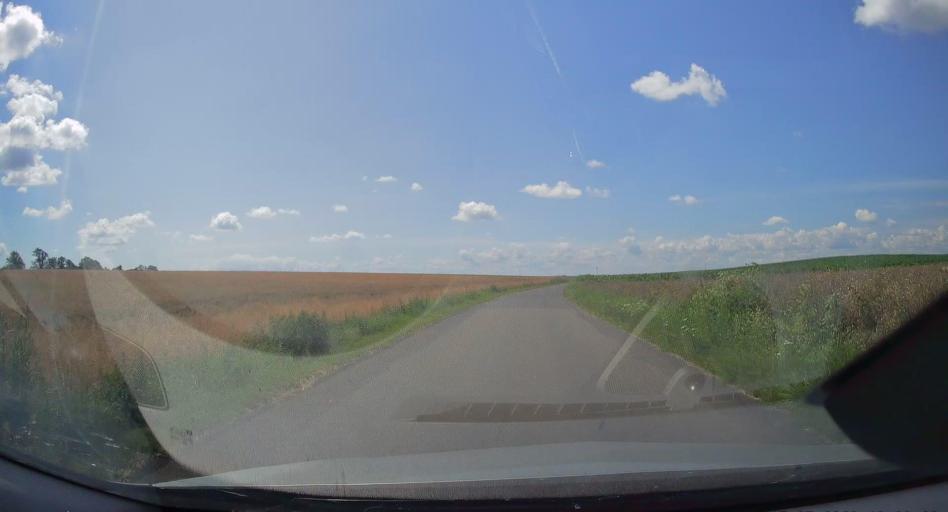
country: PL
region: Subcarpathian Voivodeship
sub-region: Powiat jaroslawski
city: Sosnica
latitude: 49.8577
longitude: 22.8802
